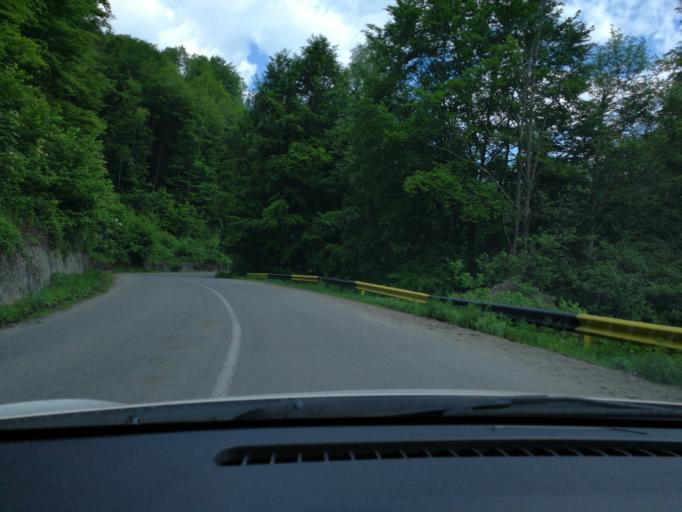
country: RO
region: Prahova
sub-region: Comuna Valea Doftanei
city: Tesila
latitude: 45.2693
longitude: 25.7328
